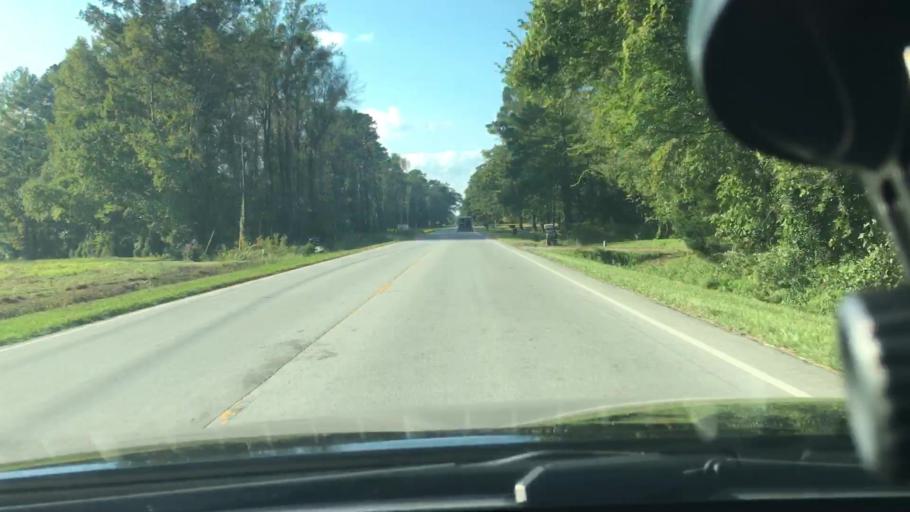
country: US
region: North Carolina
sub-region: Craven County
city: Vanceboro
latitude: 35.2599
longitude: -77.1001
